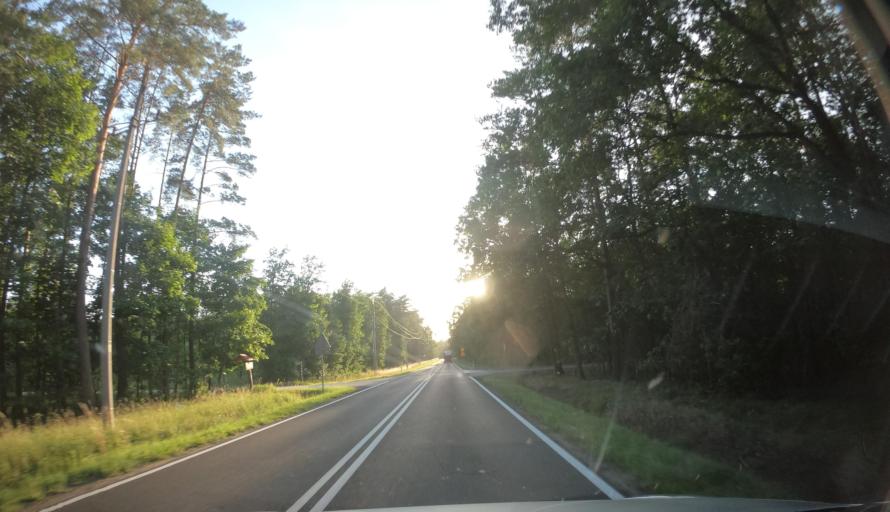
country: PL
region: Kujawsko-Pomorskie
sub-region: Powiat bydgoski
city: Koronowo
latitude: 53.3108
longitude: 18.0326
